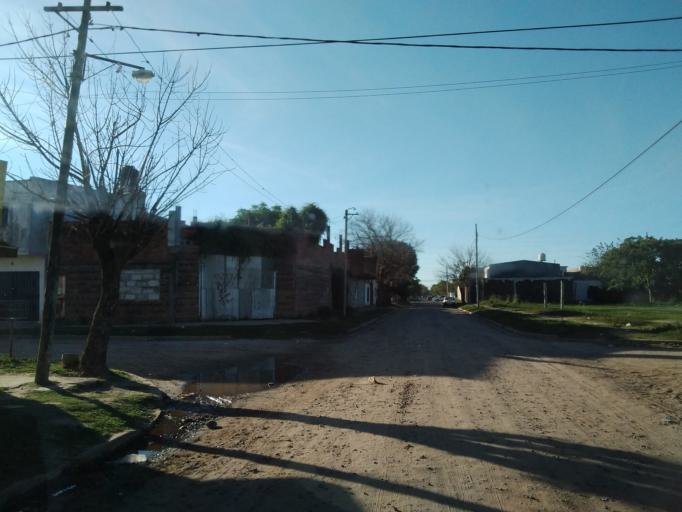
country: AR
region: Corrientes
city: Corrientes
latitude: -27.4995
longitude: -58.8356
